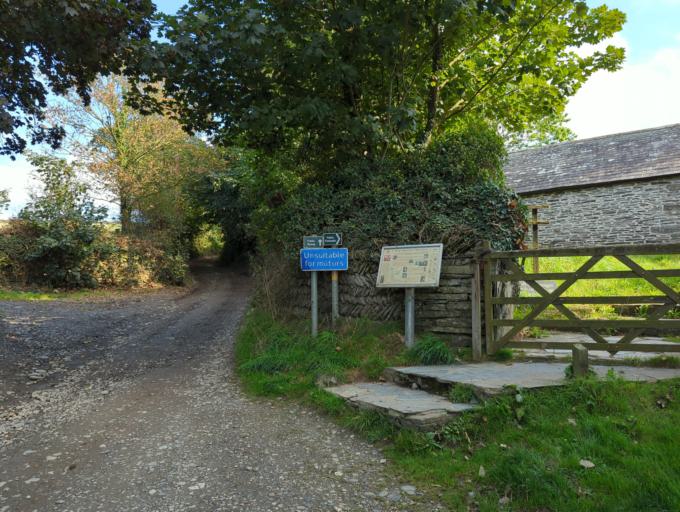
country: GB
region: England
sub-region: Cornwall
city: Tintagel
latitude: 50.6706
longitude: -4.7234
